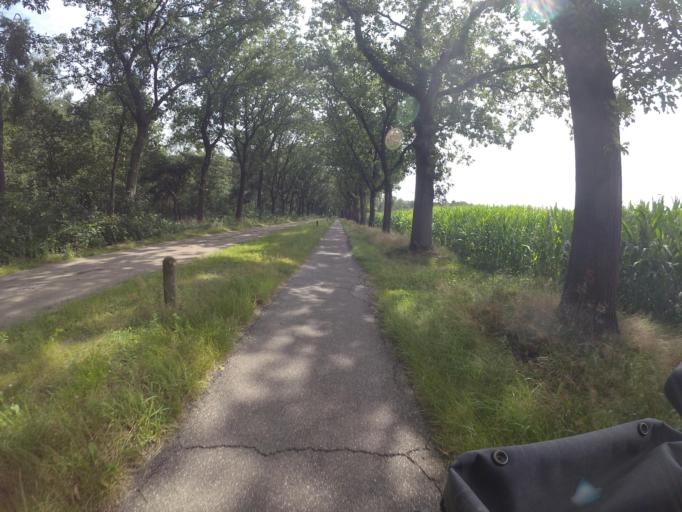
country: NL
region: North Brabant
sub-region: Bergeijk
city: Bergeyk
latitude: 51.3115
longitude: 5.3831
